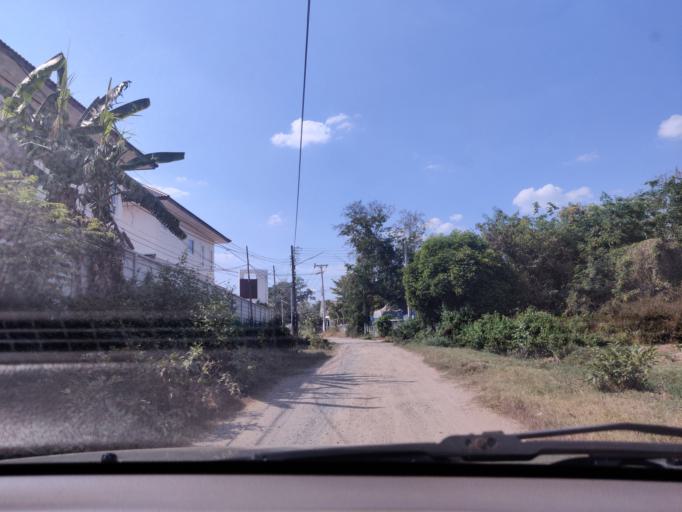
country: TH
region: Sisaket
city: Si Sa Ket
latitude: 15.1018
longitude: 104.3571
